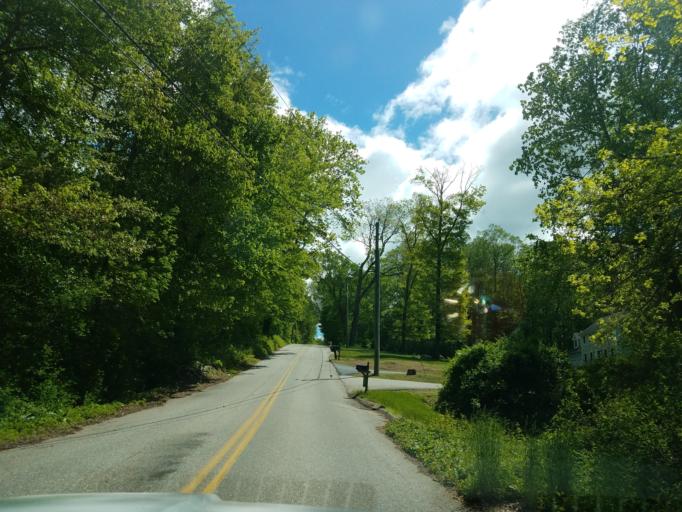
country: US
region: Connecticut
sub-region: New London County
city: Colchester
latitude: 41.5123
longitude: -72.3208
